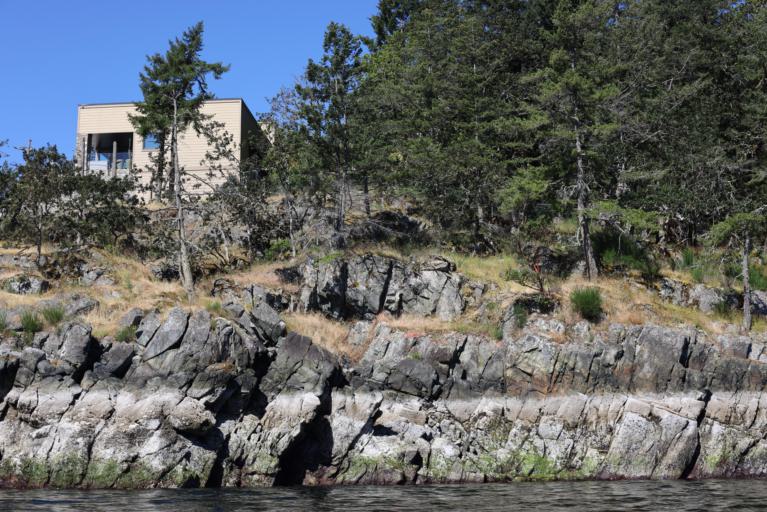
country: CA
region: British Columbia
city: North Cowichan
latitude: 48.8246
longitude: -123.5838
